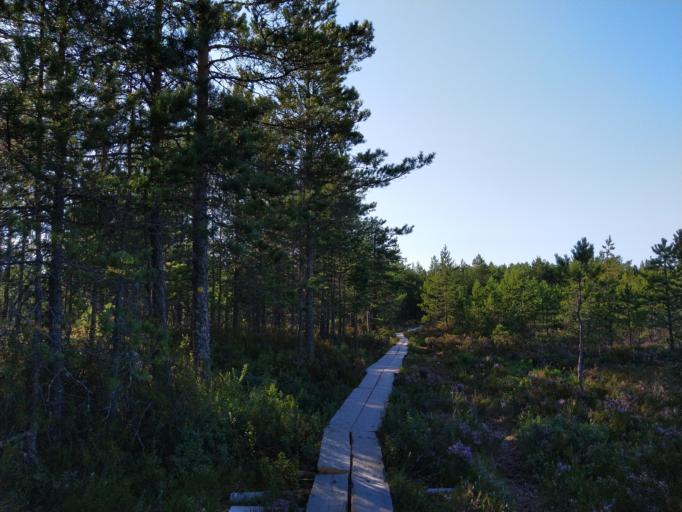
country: FI
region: Varsinais-Suomi
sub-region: Turku
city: Rusko
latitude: 60.5066
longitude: 22.2547
